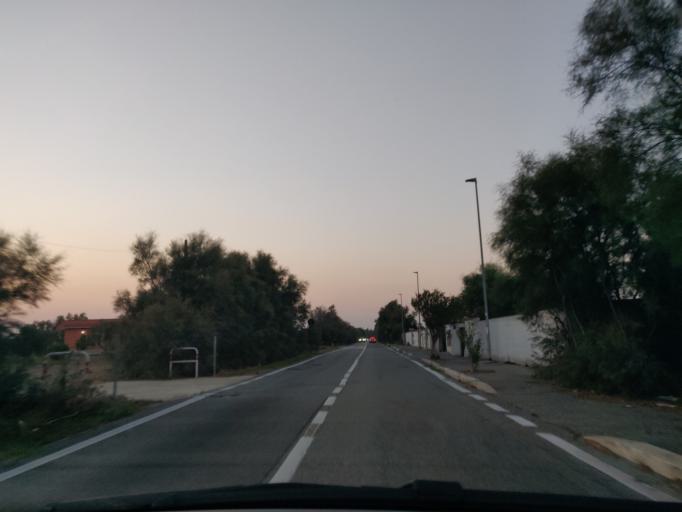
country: IT
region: Latium
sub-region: Citta metropolitana di Roma Capitale
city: Npp 23 (Parco Leonardo)
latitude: 41.8209
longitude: 12.2939
